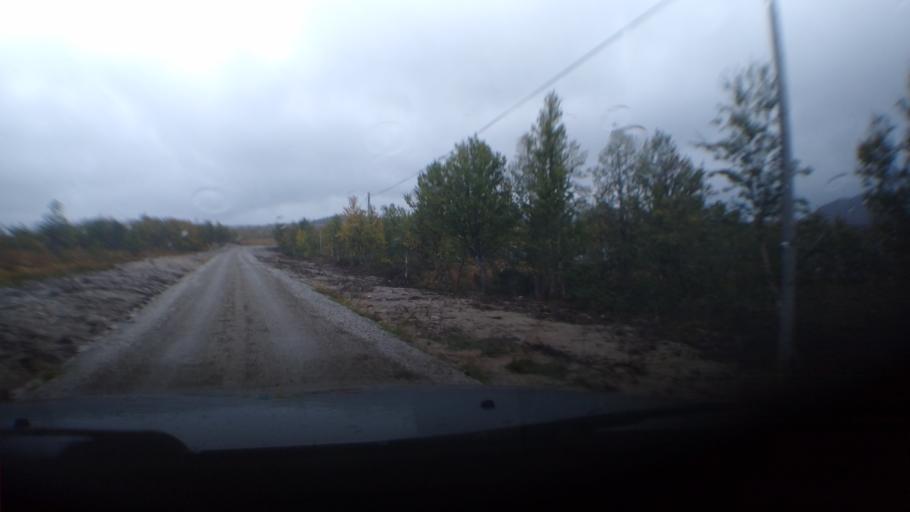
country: NO
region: Oppland
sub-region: Ringebu
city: Ringebu
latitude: 61.6586
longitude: 10.1038
